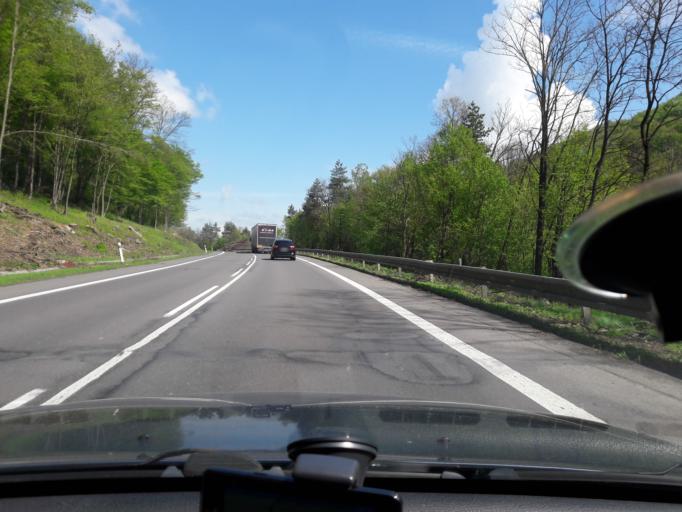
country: SK
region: Banskobystricky
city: Krupina
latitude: 48.4035
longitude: 19.0863
